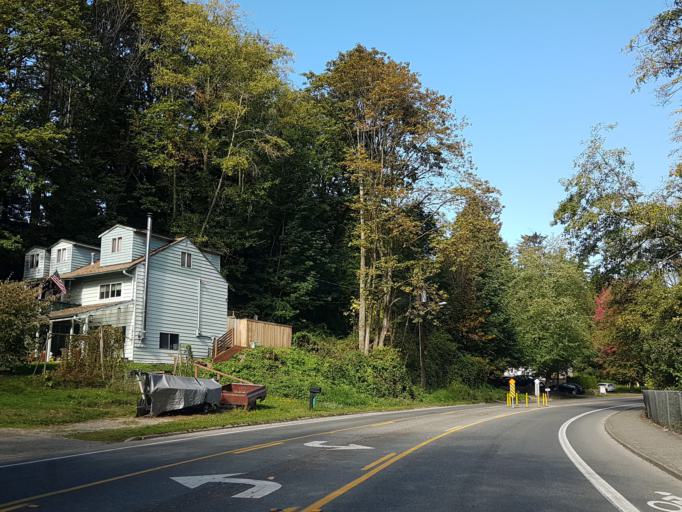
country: US
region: Washington
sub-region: King County
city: Lake Forest Park
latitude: 47.7615
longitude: -122.2634
